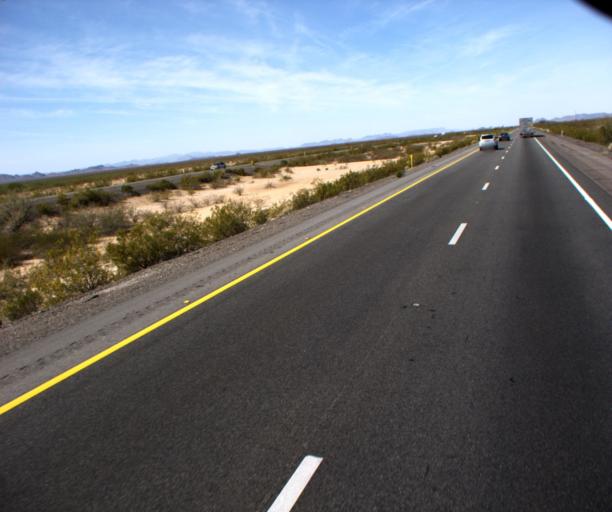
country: US
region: Arizona
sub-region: La Paz County
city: Salome
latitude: 33.5797
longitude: -113.4220
